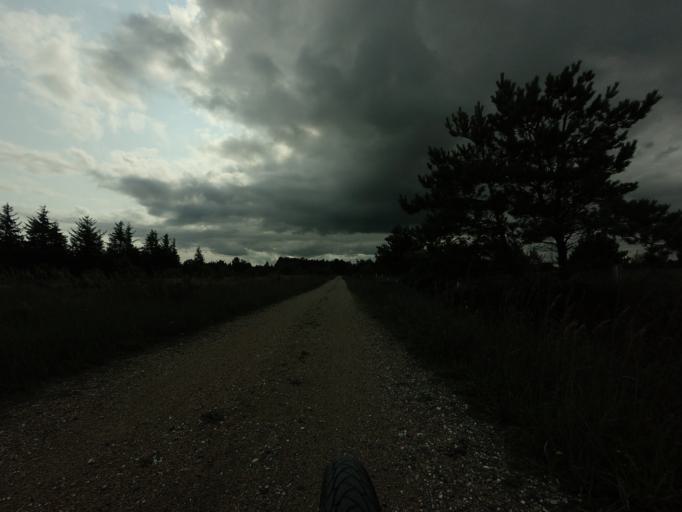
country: DK
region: North Denmark
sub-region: Frederikshavn Kommune
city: Strandby
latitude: 57.6297
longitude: 10.4021
